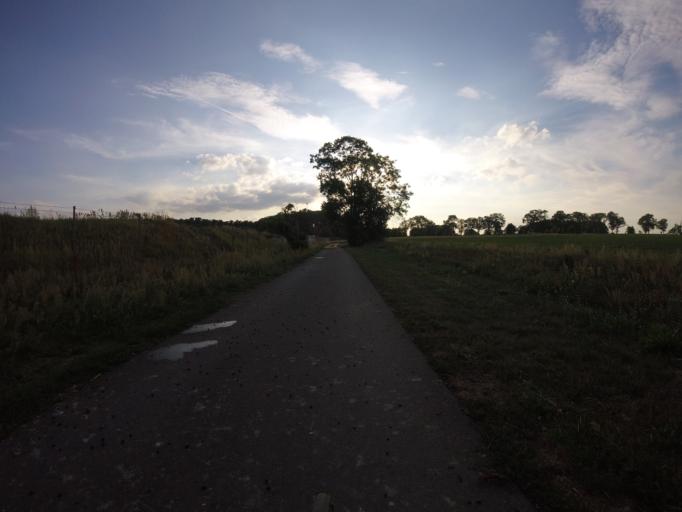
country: DE
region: Brandenburg
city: Neuenhagen
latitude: 52.5776
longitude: 13.6761
